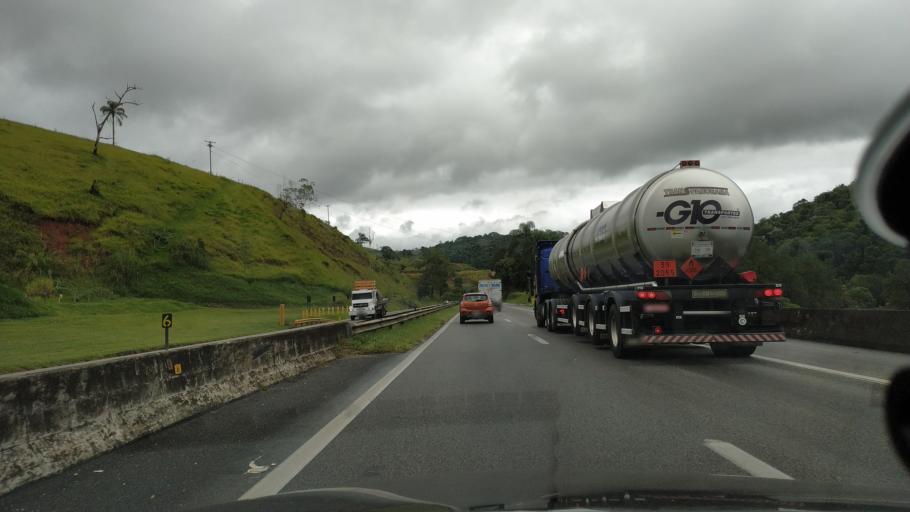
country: BR
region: Sao Paulo
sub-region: Santa Isabel
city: Santa Isabel
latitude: -23.3541
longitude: -46.2028
